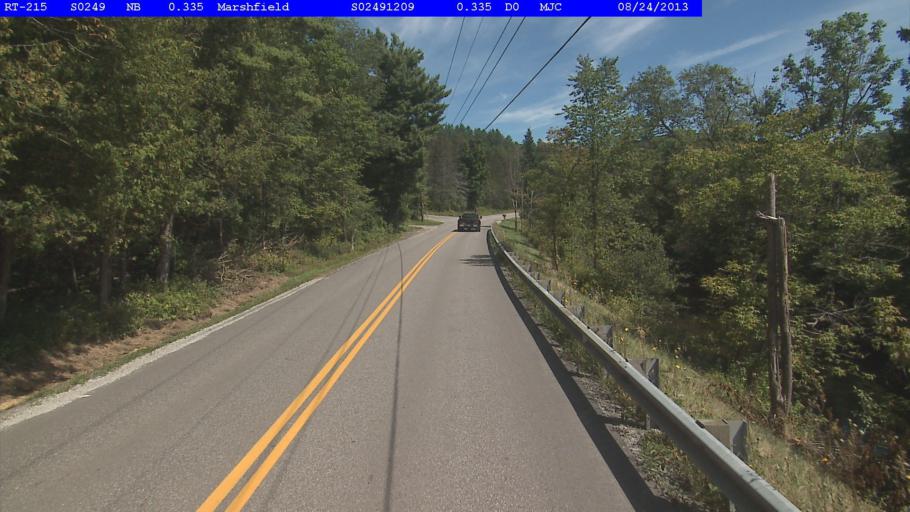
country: US
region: Vermont
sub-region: Caledonia County
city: Hardwick
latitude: 44.3554
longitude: -72.3450
